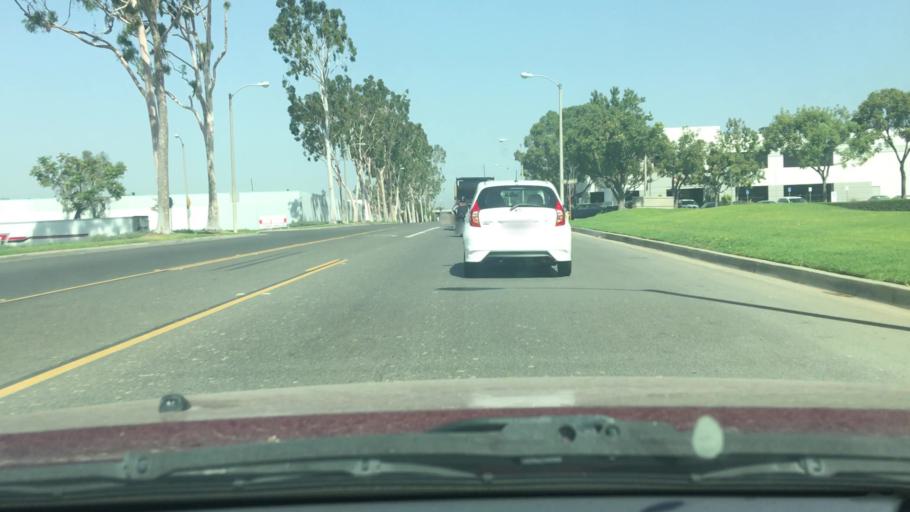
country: US
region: California
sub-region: Orange County
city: Buena Park
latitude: 33.8851
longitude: -118.0158
